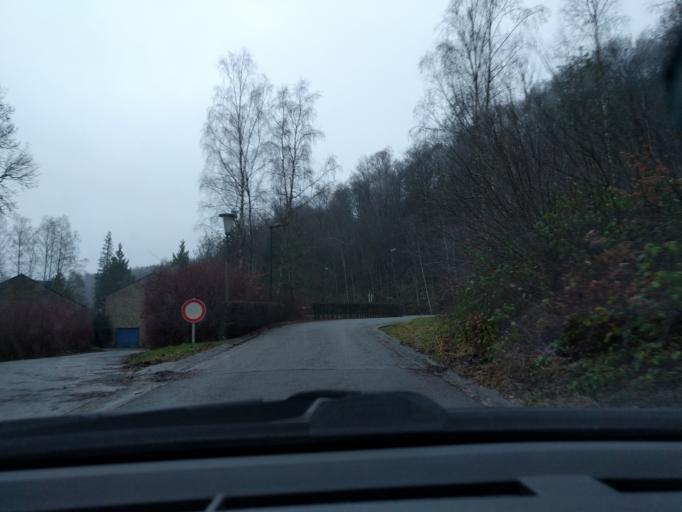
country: BE
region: Wallonia
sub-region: Province de Namur
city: Couvin
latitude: 50.0239
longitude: 4.5334
